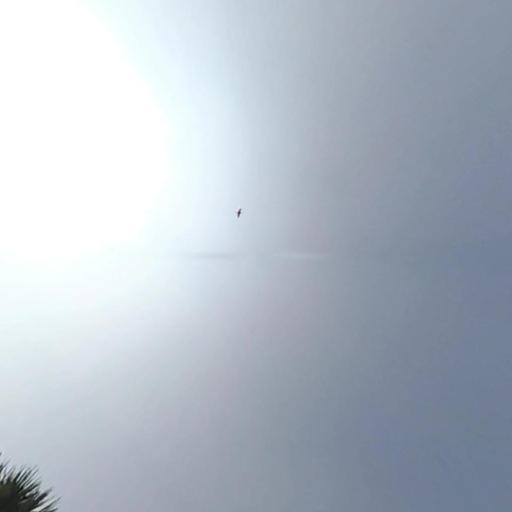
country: IN
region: Telangana
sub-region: Nalgonda
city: Nalgonda
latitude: 17.1964
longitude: 79.1377
